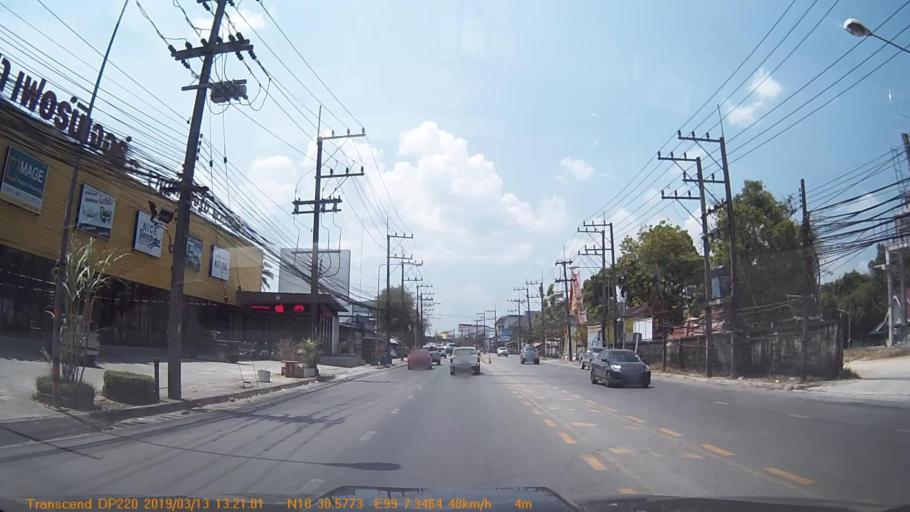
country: TH
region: Chumphon
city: Chumphon
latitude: 10.5088
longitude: 99.1238
